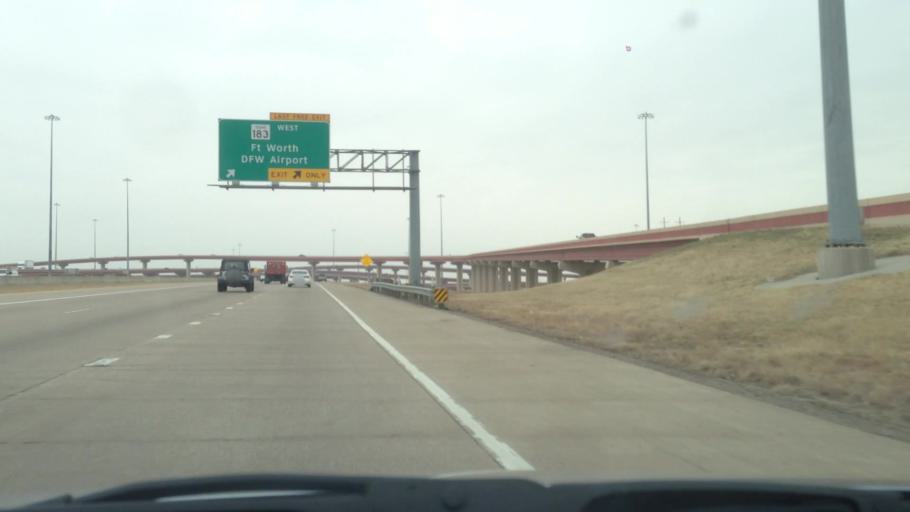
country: US
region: Texas
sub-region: Tarrant County
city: Euless
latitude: 32.8437
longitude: -97.0171
